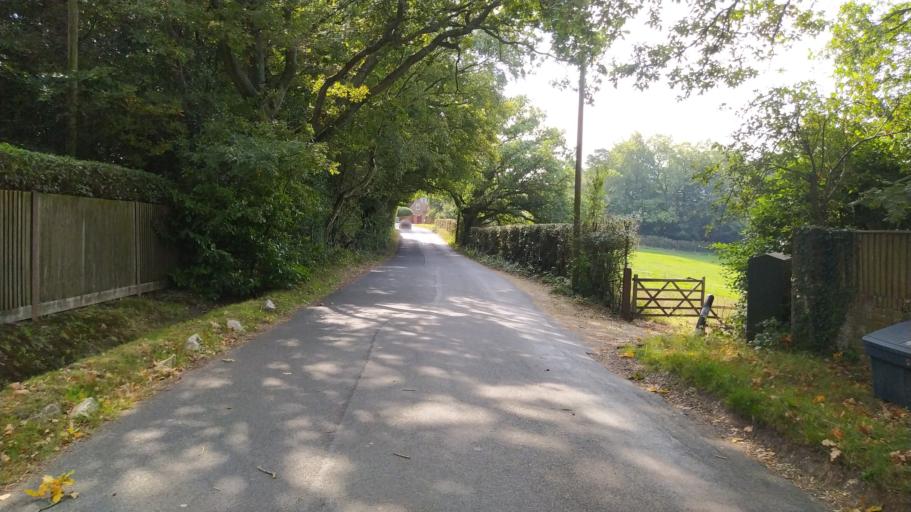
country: GB
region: England
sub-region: Surrey
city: Farnham
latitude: 51.2370
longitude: -0.8337
